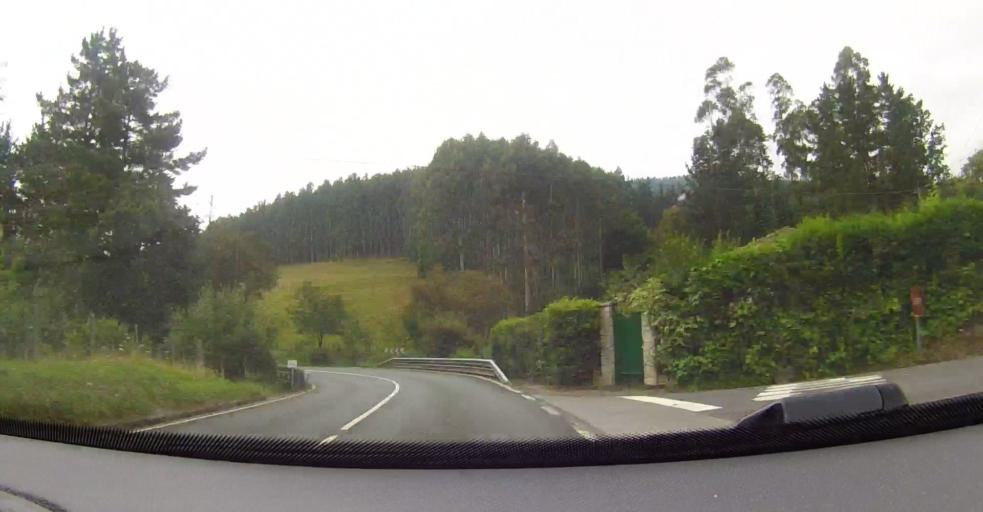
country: ES
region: Basque Country
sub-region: Bizkaia
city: Balmaseda
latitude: 43.2314
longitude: -3.1989
